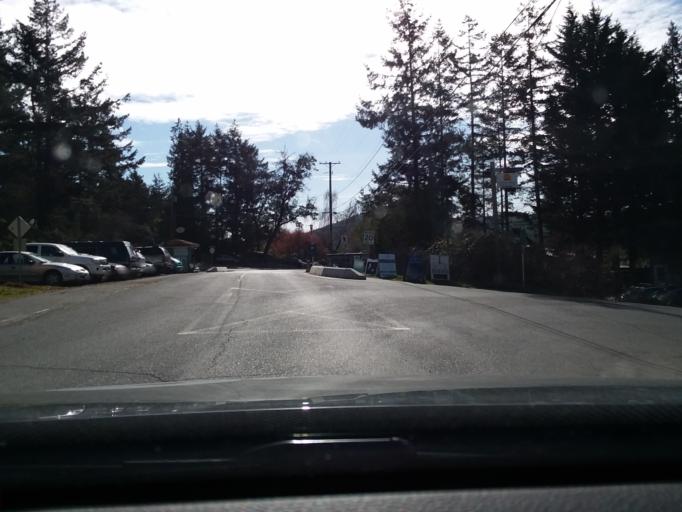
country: CA
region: British Columbia
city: North Saanich
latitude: 48.8789
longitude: -123.3180
